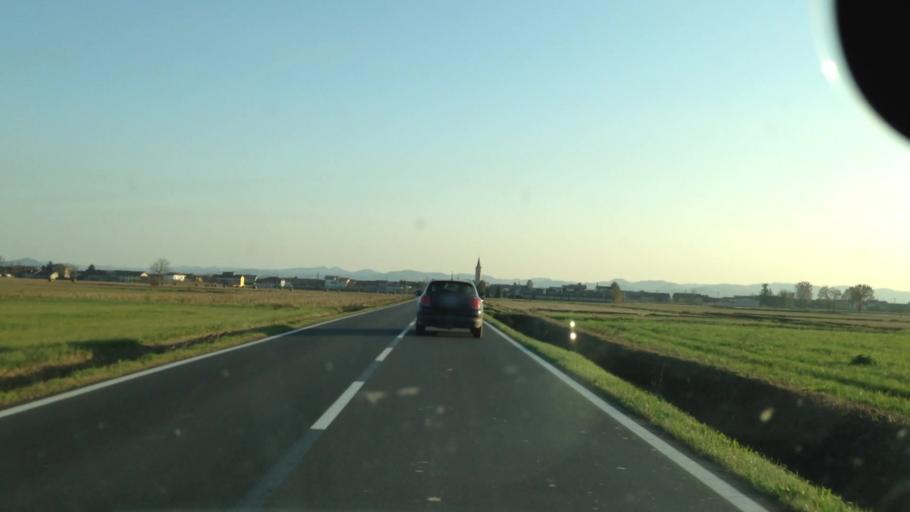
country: IT
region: Piedmont
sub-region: Provincia di Vercelli
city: Lamporo
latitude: 45.2378
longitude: 8.0942
